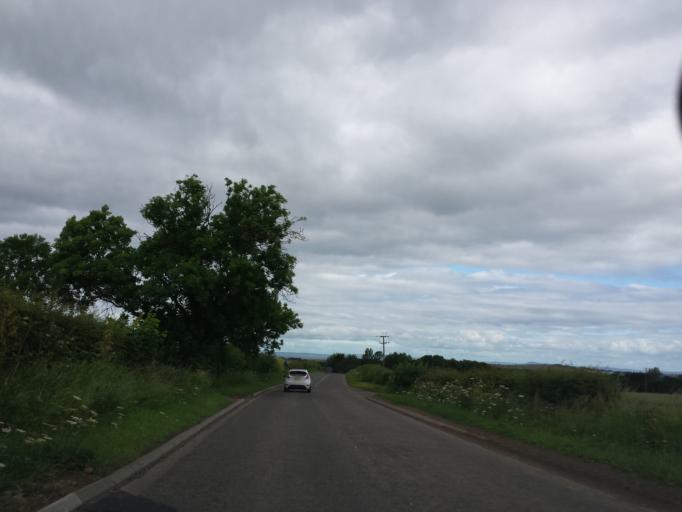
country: GB
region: Scotland
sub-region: East Lothian
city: Gullane
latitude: 55.9876
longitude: -2.8282
